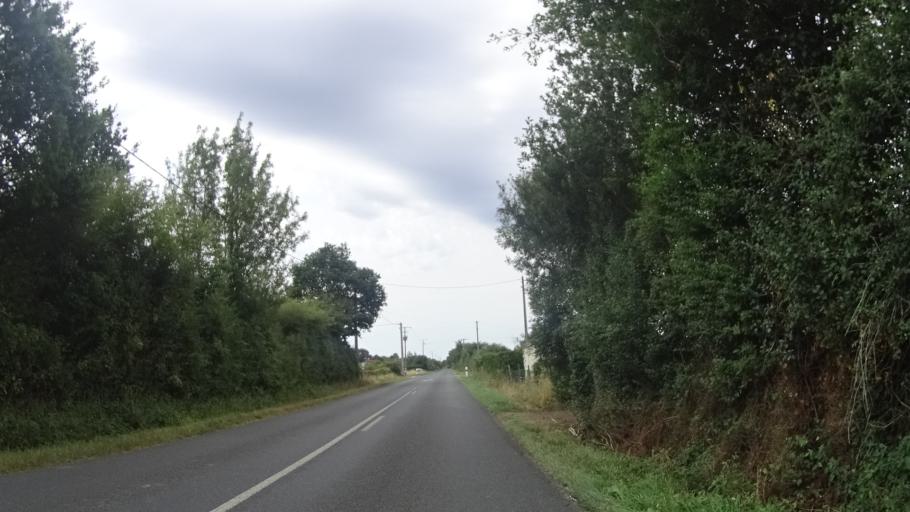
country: FR
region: Pays de la Loire
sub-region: Departement de la Loire-Atlantique
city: Heric
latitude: 47.4643
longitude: -1.6829
